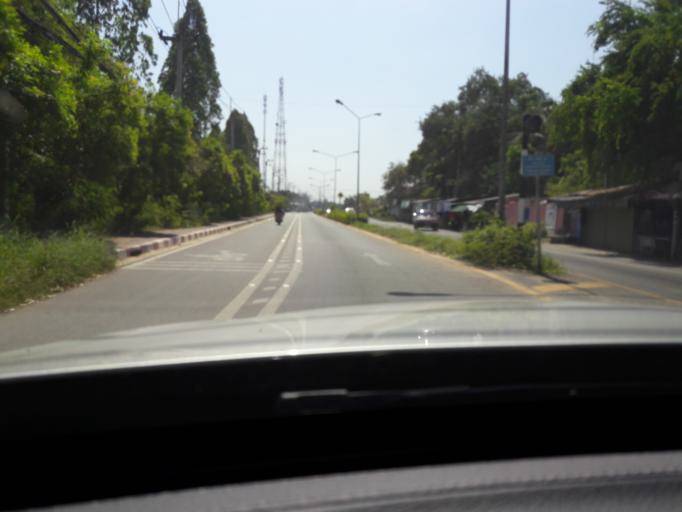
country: TH
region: Phetchaburi
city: Cha-am
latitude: 12.8200
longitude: 99.9830
